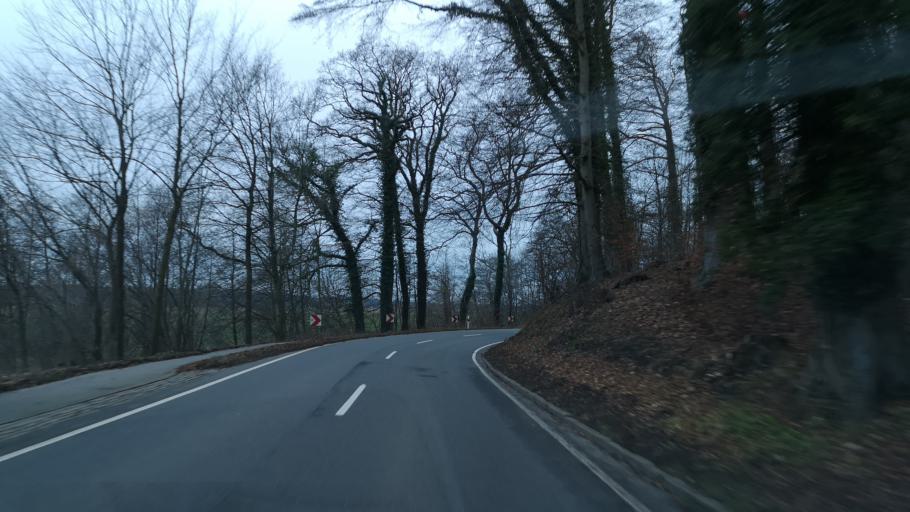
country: DE
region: Schleswig-Holstein
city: Munsterdorf
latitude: 53.9137
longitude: 9.5427
